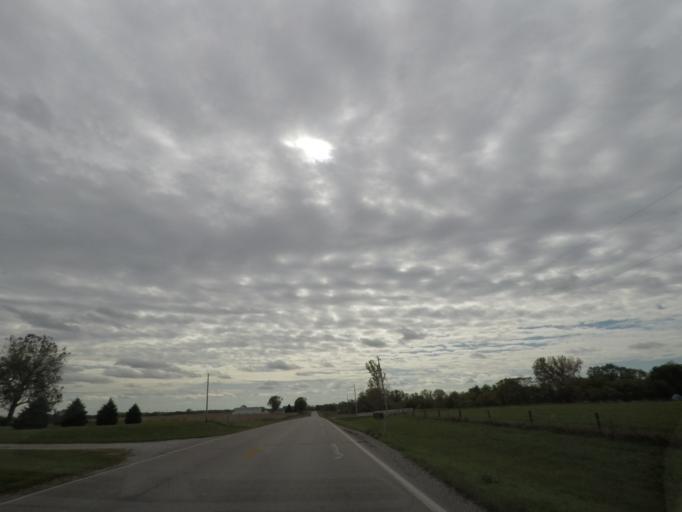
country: US
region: Iowa
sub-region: Story County
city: Huxley
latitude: 41.8472
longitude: -93.5316
